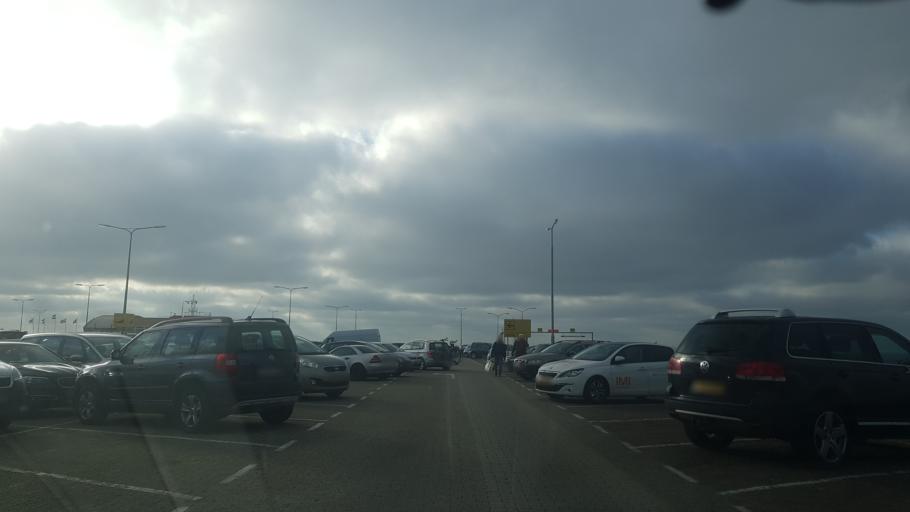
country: NL
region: Friesland
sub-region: Gemeente Dongeradeel
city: Holwerd
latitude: 53.3937
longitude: 5.8826
